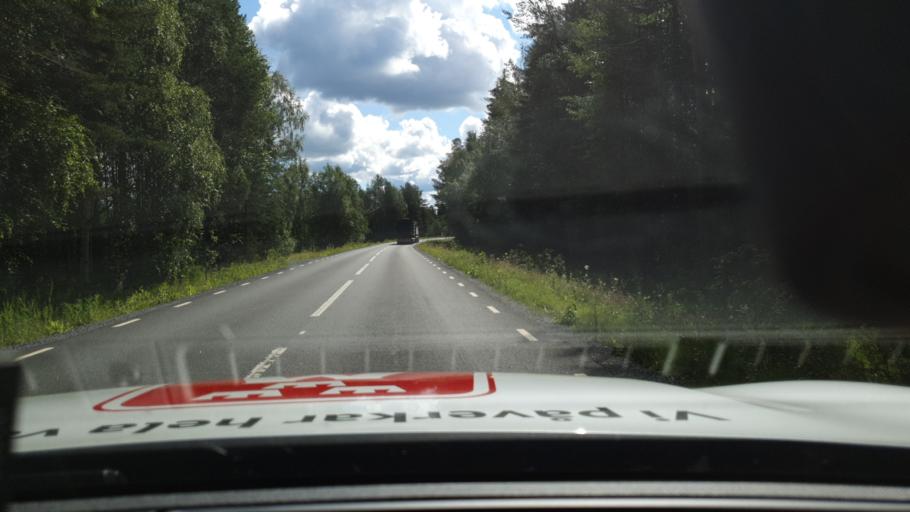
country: SE
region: Norrbotten
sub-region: Bodens Kommun
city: Boden
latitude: 65.8463
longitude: 21.7353
